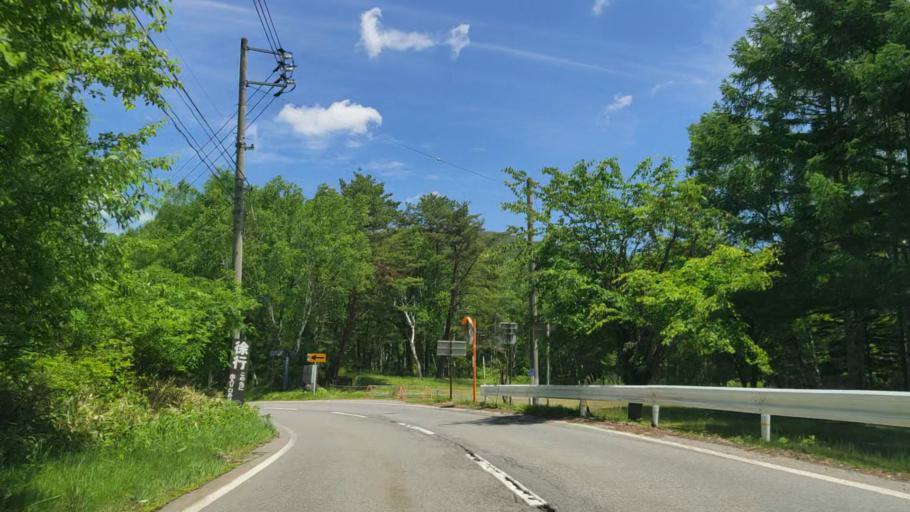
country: JP
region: Nagano
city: Suwa
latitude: 36.1213
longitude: 138.2302
